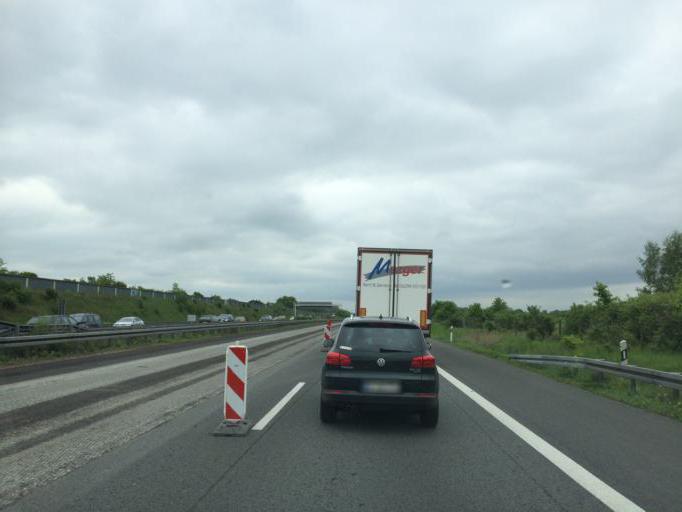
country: DE
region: Lower Saxony
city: Klein Schwulper
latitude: 52.3333
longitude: 10.4307
